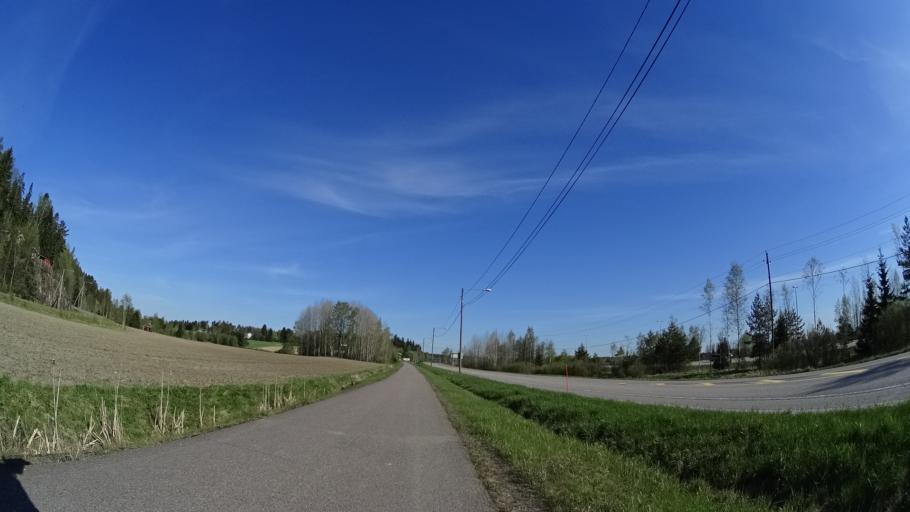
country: FI
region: Uusimaa
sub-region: Helsinki
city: Nurmijaervi
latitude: 60.3404
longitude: 24.8144
